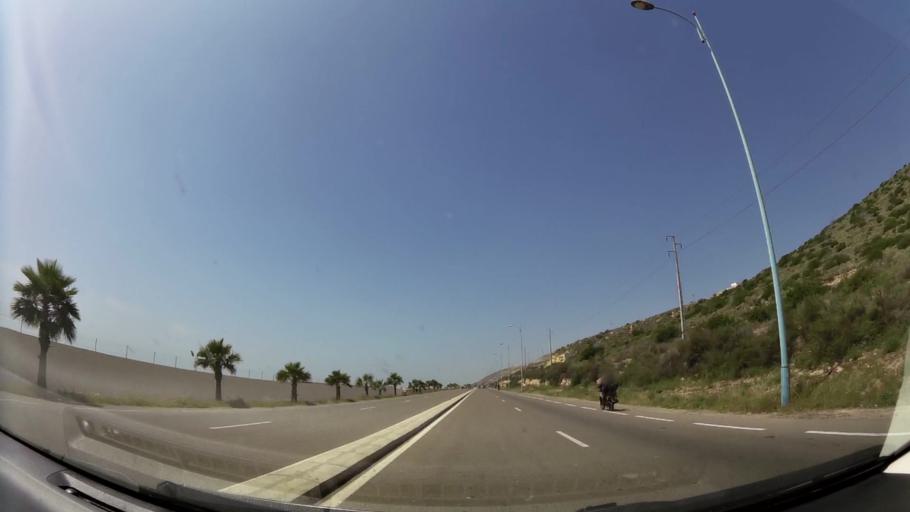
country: MA
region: Souss-Massa-Draa
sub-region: Agadir-Ida-ou-Tnan
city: Agadir
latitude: 30.4410
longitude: -9.6403
